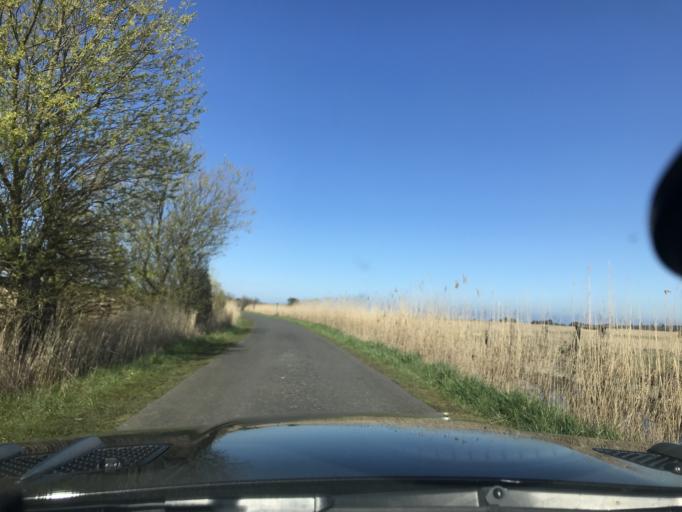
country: DE
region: Schleswig-Holstein
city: Heiligenhafen
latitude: 54.4646
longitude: 11.0198
